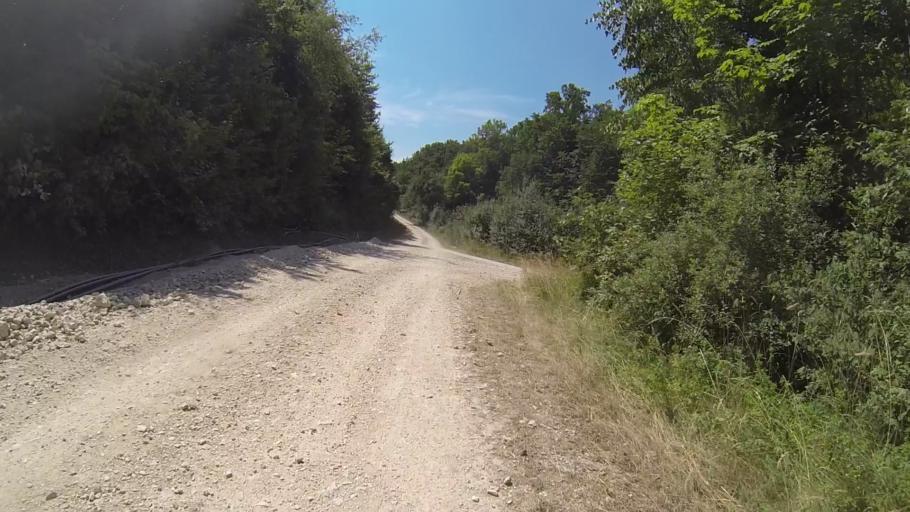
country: DE
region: Baden-Wuerttemberg
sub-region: Regierungsbezirk Stuttgart
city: Giengen an der Brenz
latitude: 48.6422
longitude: 10.2162
